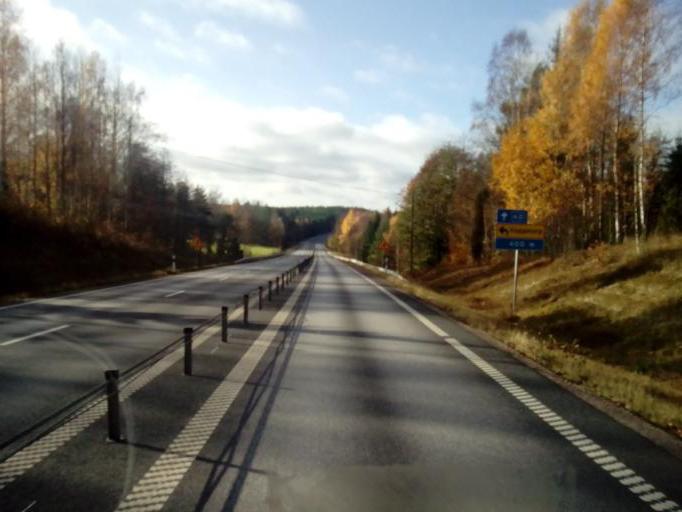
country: SE
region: Kalmar
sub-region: Vimmerby Kommun
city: Vimmerby
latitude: 57.6749
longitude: 15.9365
